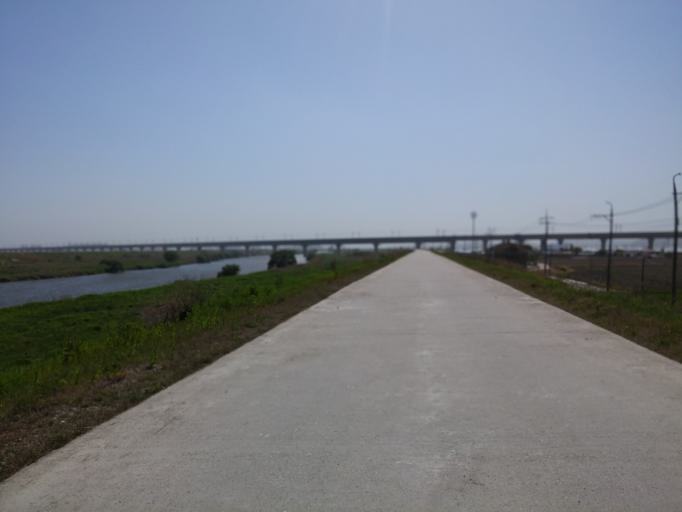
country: KR
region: Chungcheongnam-do
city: Nonsan
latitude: 36.1834
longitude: 127.0480
